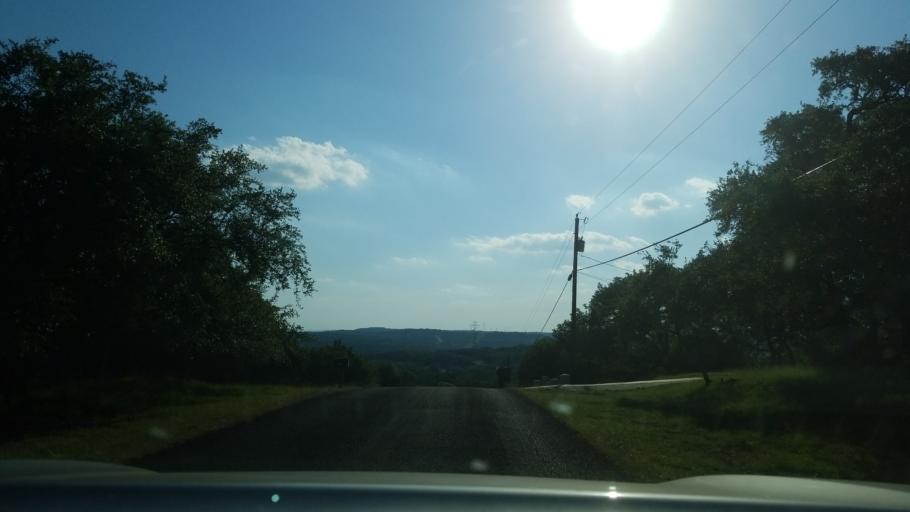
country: US
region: Texas
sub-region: Comal County
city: Bulverde
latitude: 29.7828
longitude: -98.4506
